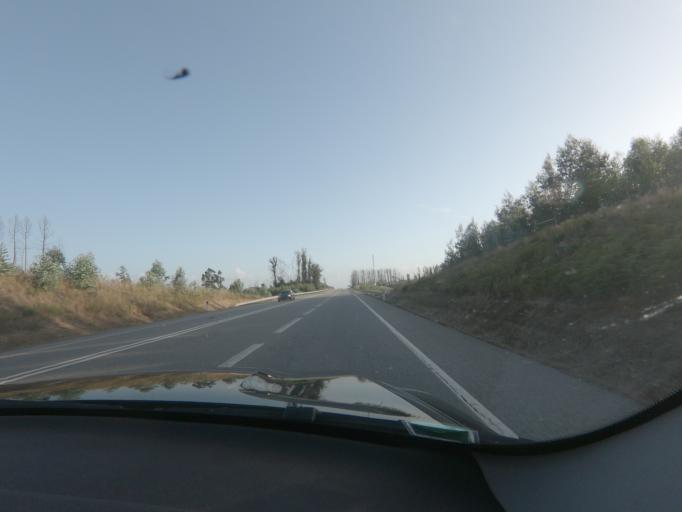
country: PT
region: Viseu
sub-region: Concelho de Tondela
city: Tondela
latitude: 40.4715
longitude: -8.0959
